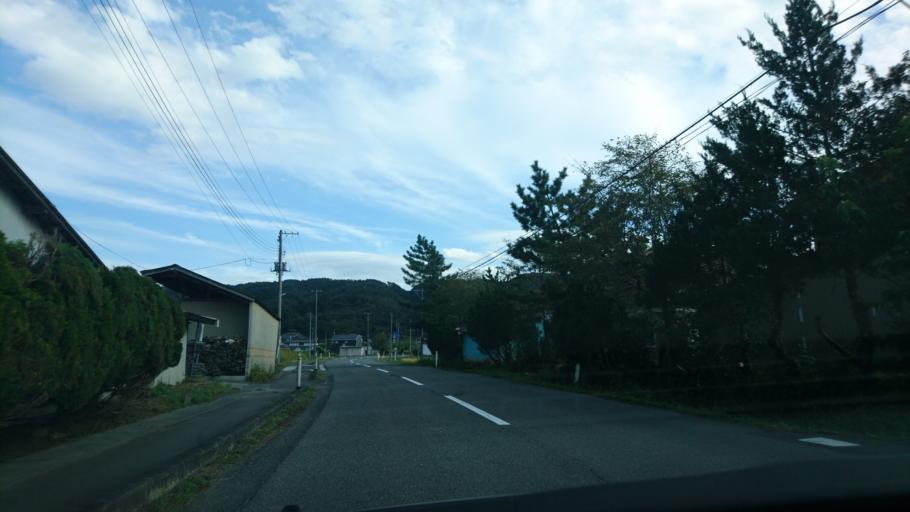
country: JP
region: Iwate
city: Ichinoseki
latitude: 38.8317
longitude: 141.2515
